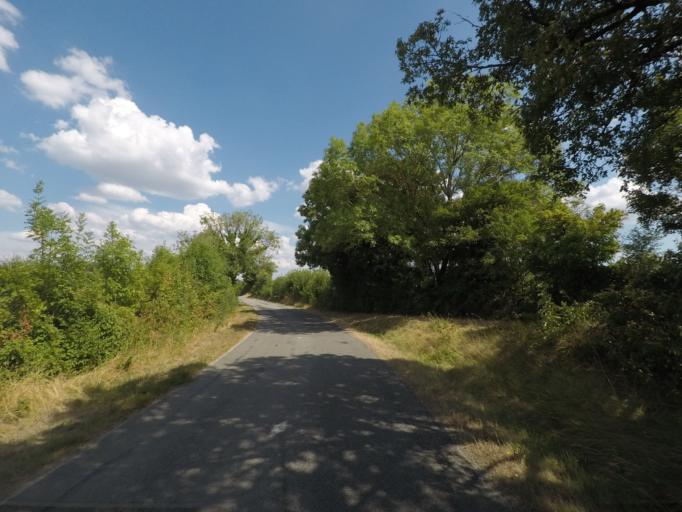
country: FR
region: Midi-Pyrenees
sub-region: Departement du Lot
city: Le Vigan
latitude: 44.6163
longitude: 1.5968
